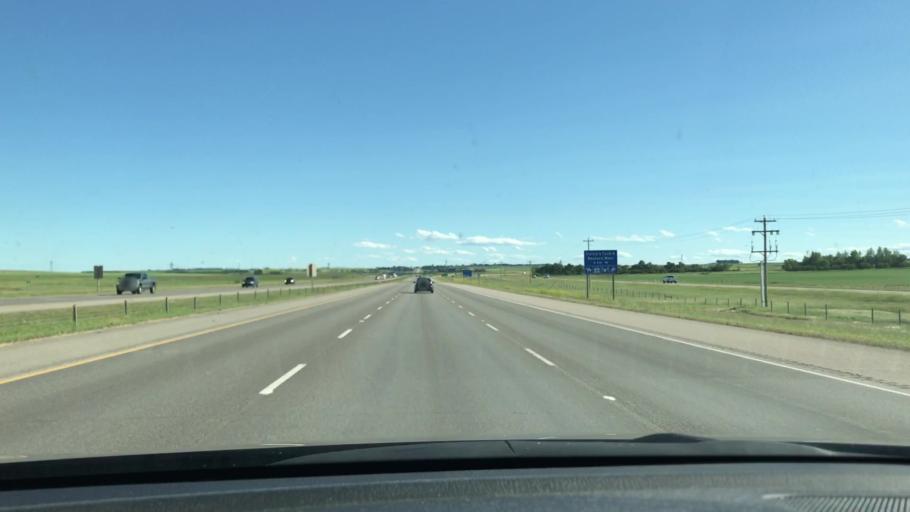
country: CA
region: Alberta
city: Crossfield
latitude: 51.4869
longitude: -114.0251
